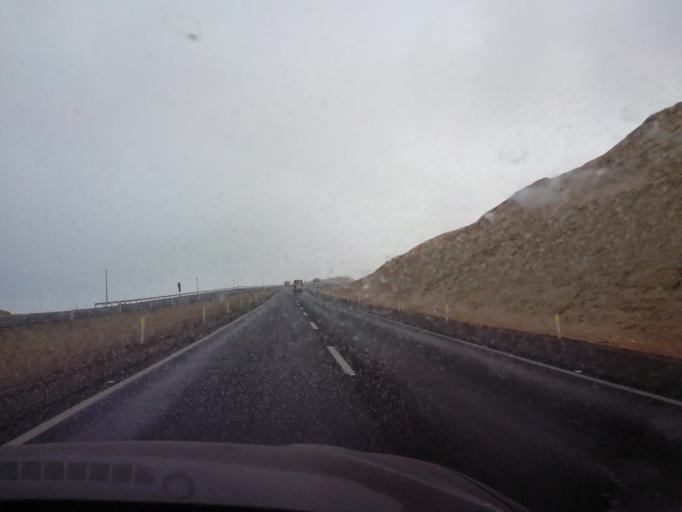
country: PE
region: Ica
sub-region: Provincia de Chincha
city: San Pedro
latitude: -13.3047
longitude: -76.2537
